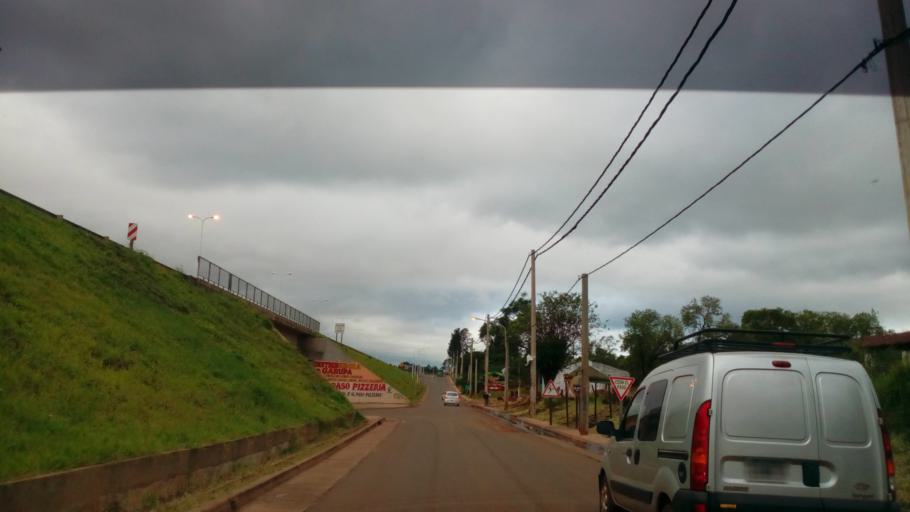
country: AR
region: Misiones
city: Garupa
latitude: -27.4591
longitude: -55.8509
